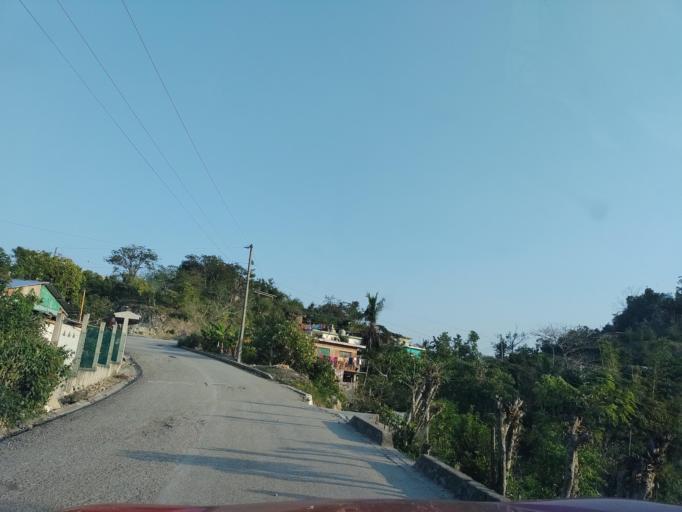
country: MX
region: Veracruz
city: Agua Dulce
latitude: 20.4047
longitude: -97.2896
